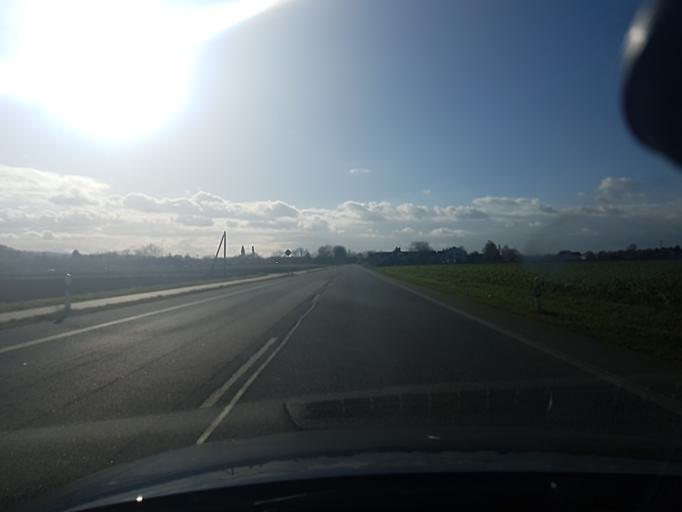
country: DE
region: Bavaria
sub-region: Lower Bavaria
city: Niederaichbach
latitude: 48.6095
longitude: 12.2863
